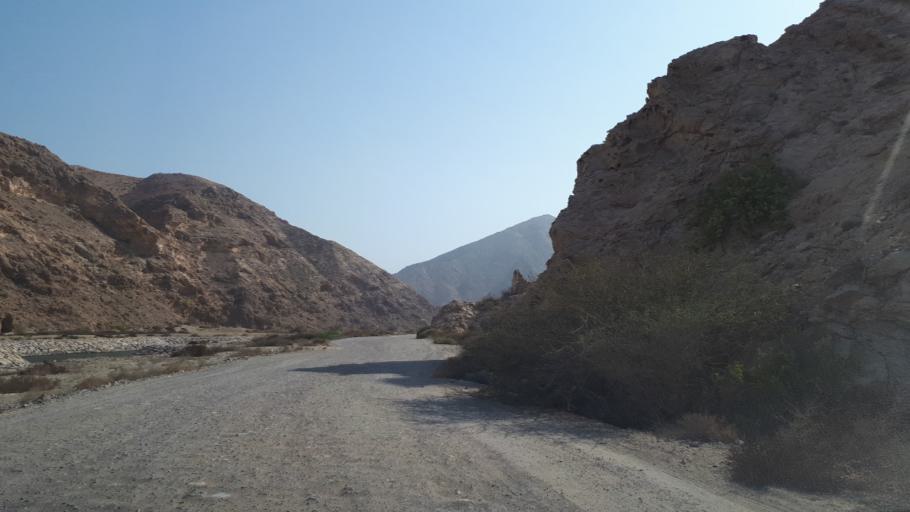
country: OM
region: Muhafazat Masqat
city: Muscat
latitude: 23.5392
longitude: 58.6567
